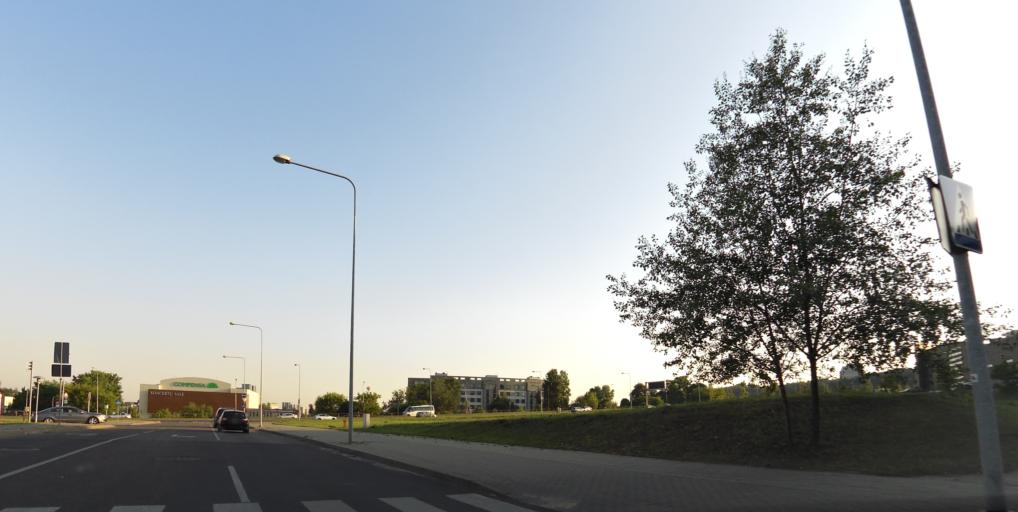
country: LT
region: Vilnius County
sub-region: Vilnius
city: Vilnius
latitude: 54.7140
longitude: 25.2764
